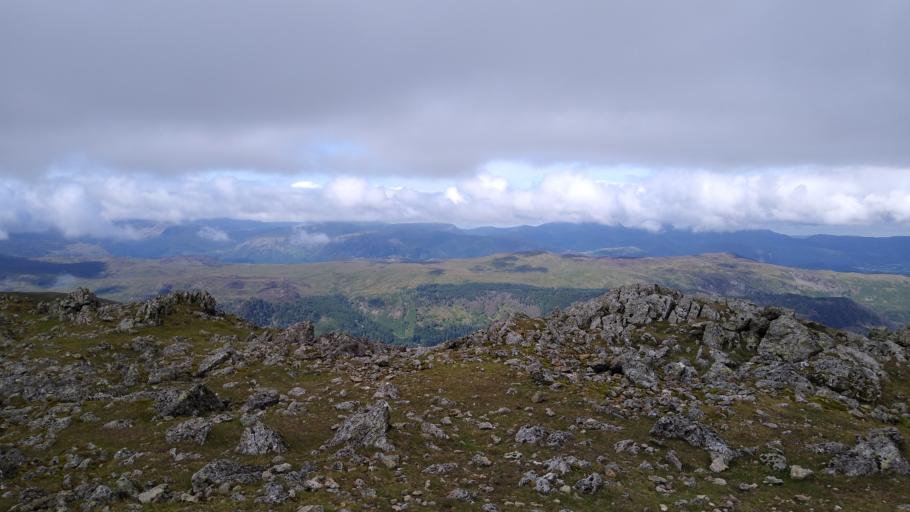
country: GB
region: England
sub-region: Cumbria
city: Keswick
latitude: 54.5477
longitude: -3.0176
